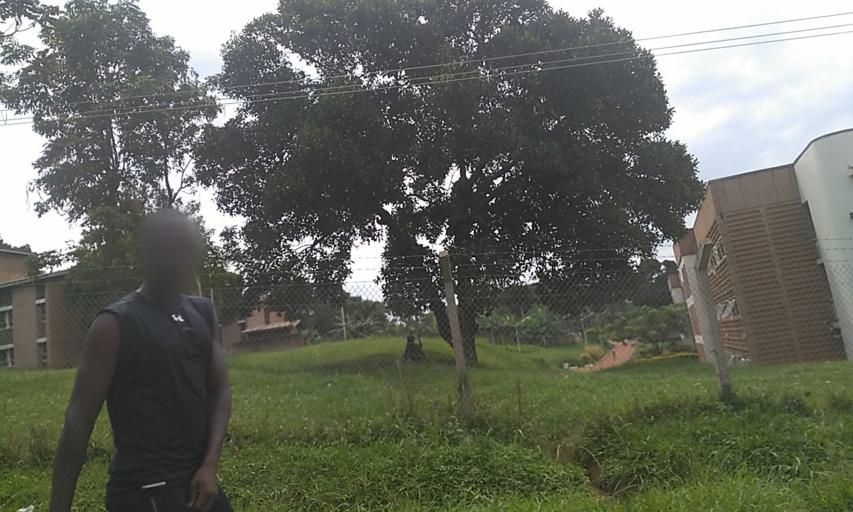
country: UG
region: Central Region
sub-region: Wakiso District
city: Kireka
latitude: 0.3522
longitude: 32.6250
